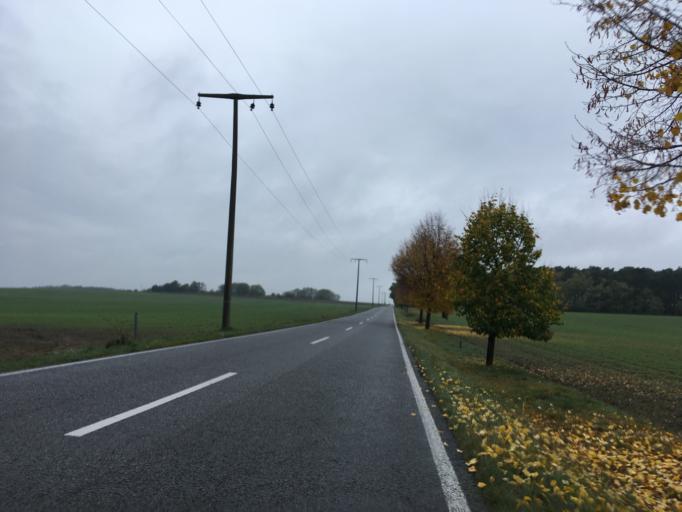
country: DE
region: Brandenburg
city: Friedland
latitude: 52.0623
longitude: 14.1882
